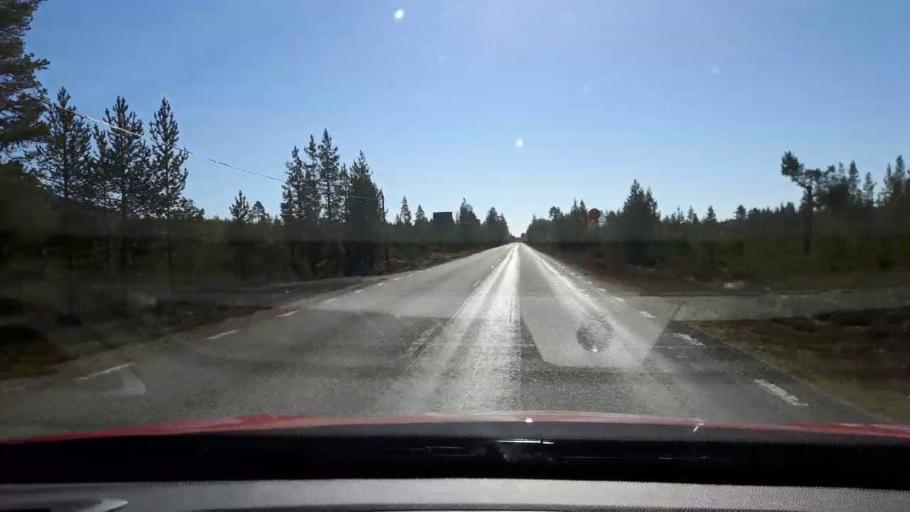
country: SE
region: Jaemtland
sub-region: Harjedalens Kommun
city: Sveg
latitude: 62.4098
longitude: 13.9216
